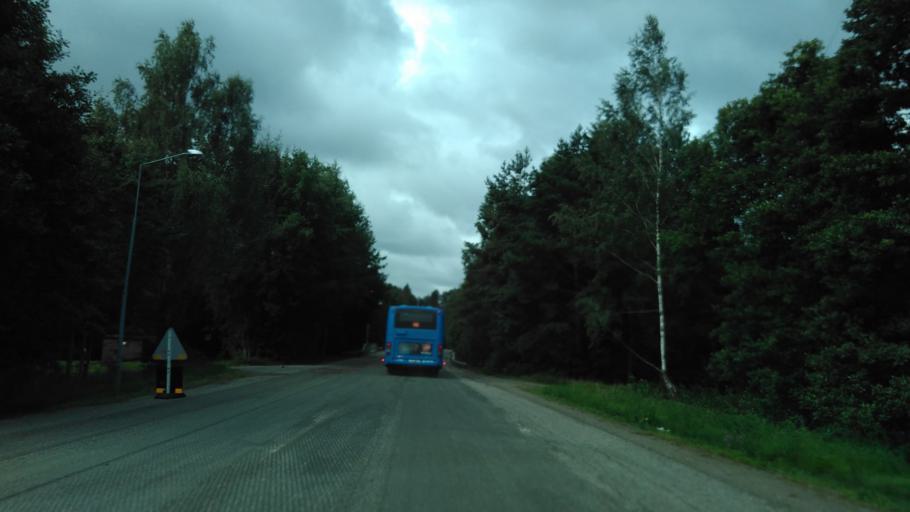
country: SE
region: Vaestra Goetaland
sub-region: Marks Kommun
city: Fritsla
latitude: 57.5609
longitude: 12.8005
